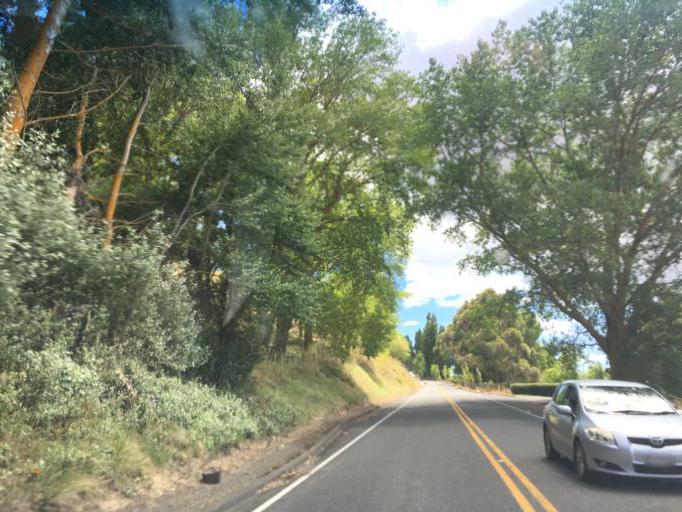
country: NZ
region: Hawke's Bay
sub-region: Hastings District
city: Hastings
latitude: -39.6871
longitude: 176.9202
